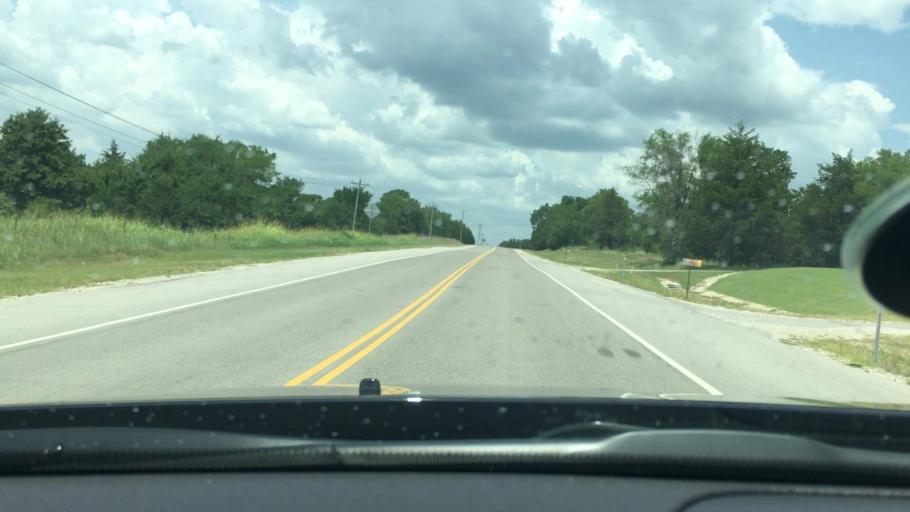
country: US
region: Oklahoma
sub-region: Love County
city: Marietta
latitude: 33.9780
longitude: -96.9872
